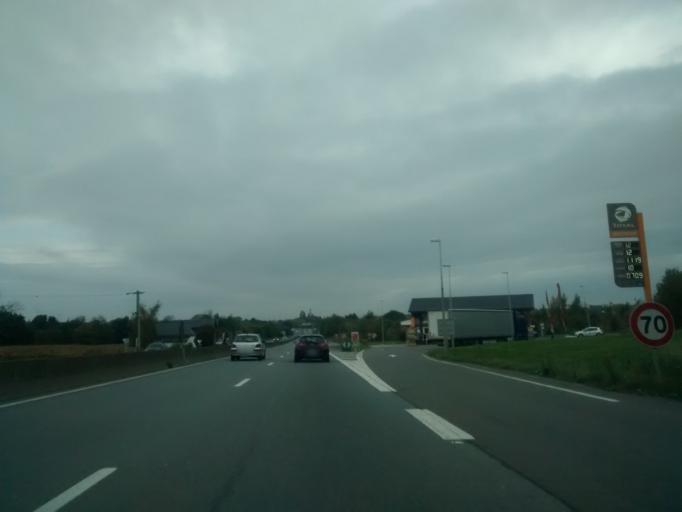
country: FR
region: Brittany
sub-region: Departement d'Ille-et-Vilaine
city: Saint-Jouan-des-Guerets
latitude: 48.6121
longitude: -1.9816
